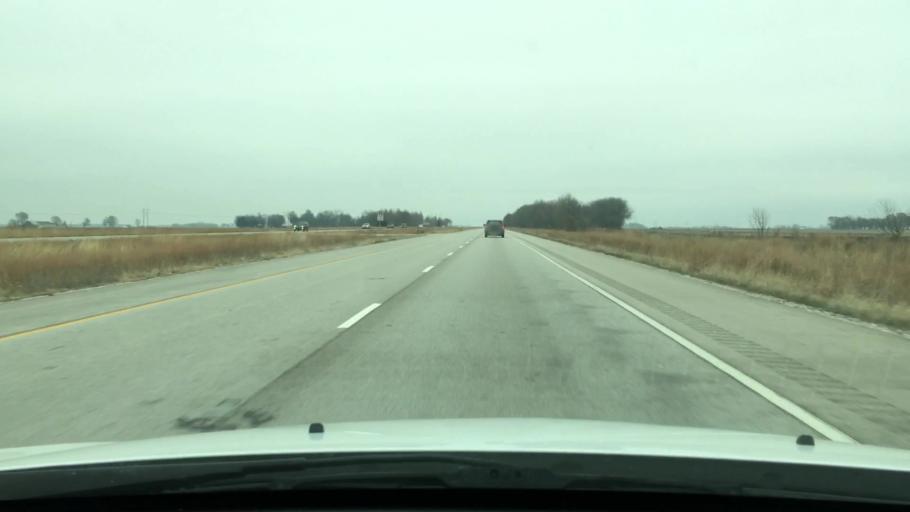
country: US
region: Illinois
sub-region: Sangamon County
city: New Berlin
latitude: 39.7368
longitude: -90.0287
